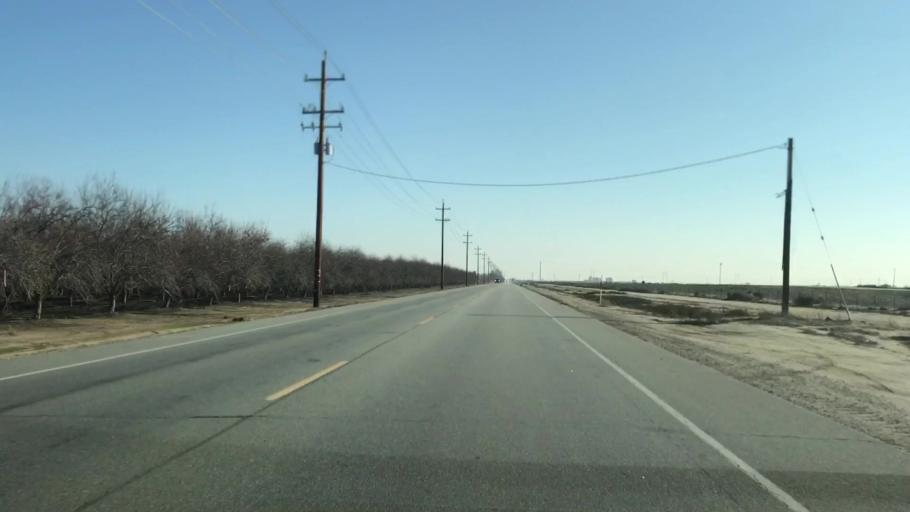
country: US
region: California
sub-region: Kern County
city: Rosedale
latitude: 35.3544
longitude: -119.2673
